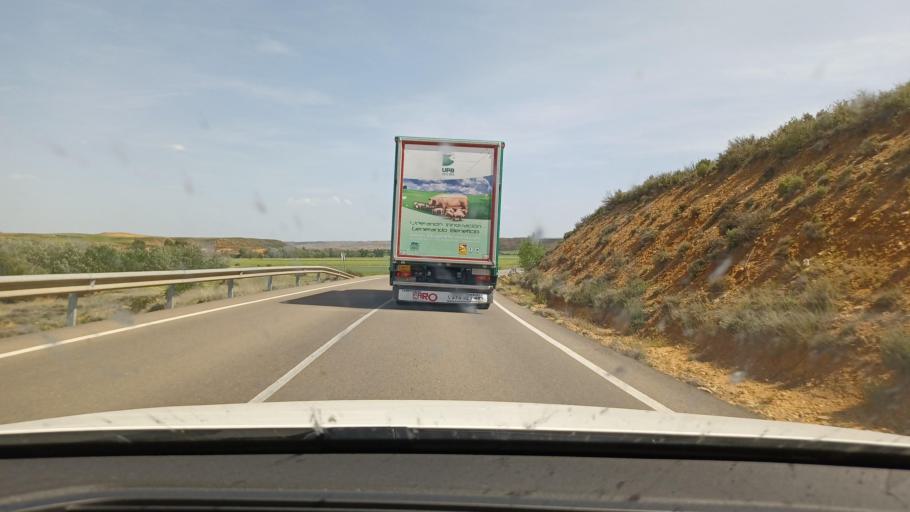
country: ES
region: Aragon
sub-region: Provincia de Zaragoza
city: Pozuel de Ariza
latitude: 41.3281
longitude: -2.1484
